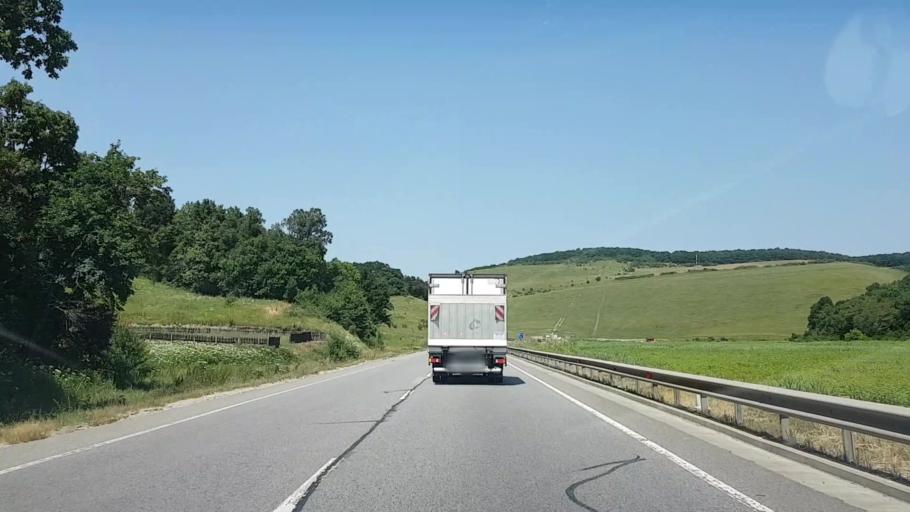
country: RO
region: Cluj
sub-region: Comuna Apahida
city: Dezmir
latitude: 46.7386
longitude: 23.7082
